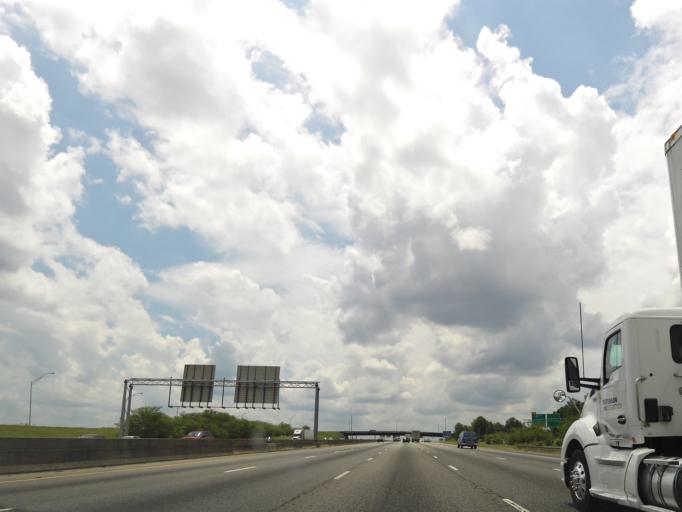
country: US
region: Georgia
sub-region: Fulton County
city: Hapeville
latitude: 33.6272
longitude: -84.4188
